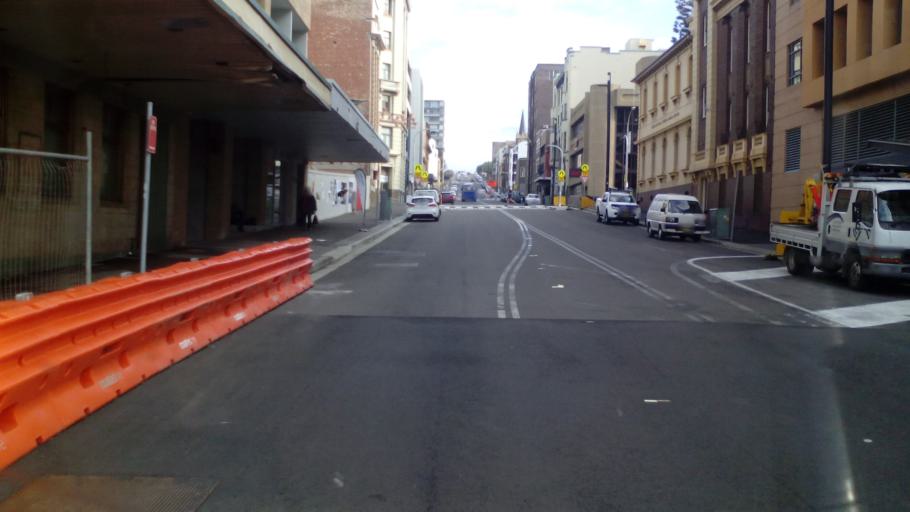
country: AU
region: New South Wales
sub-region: Newcastle
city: Newcastle
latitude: -32.9271
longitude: 151.7846
